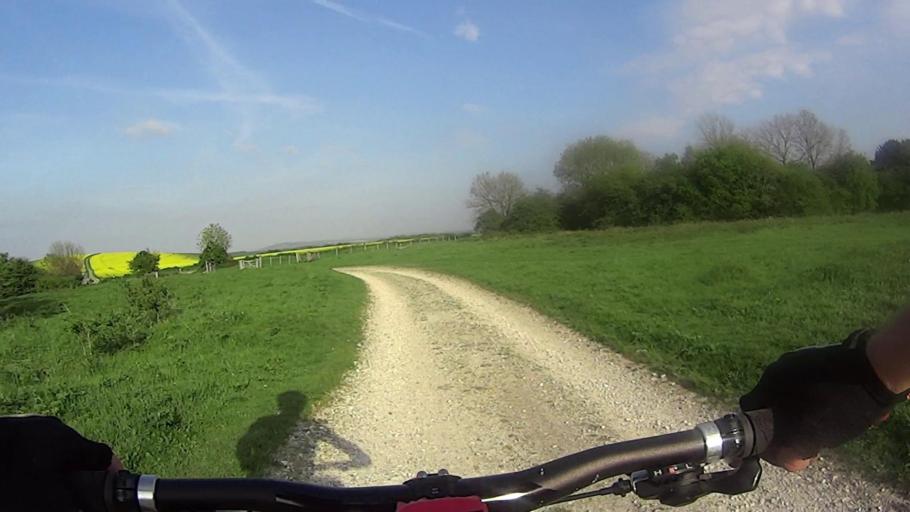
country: GB
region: England
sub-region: West Sussex
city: Fontwell
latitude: 50.9075
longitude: -0.6181
